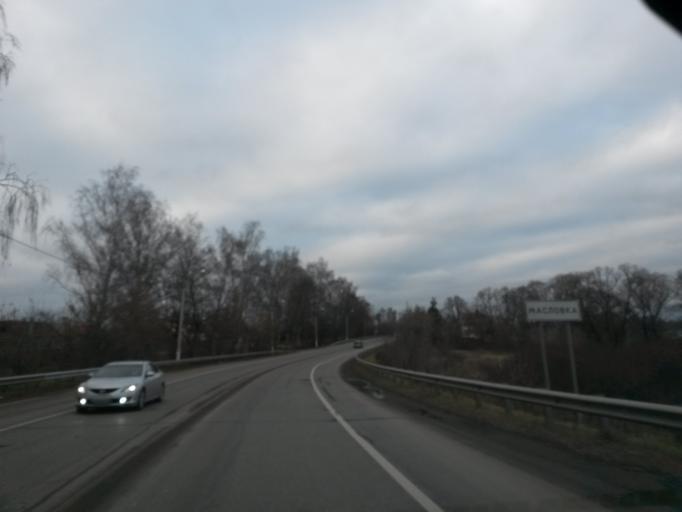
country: RU
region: Moskovskaya
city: Stolbovaya
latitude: 55.2180
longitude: 37.5034
